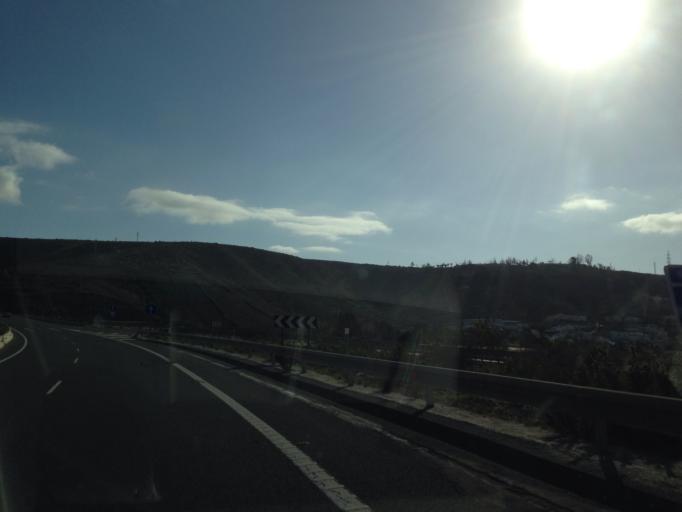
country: ES
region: Canary Islands
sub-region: Provincia de Las Palmas
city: Puerto Rico
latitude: 27.7655
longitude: -15.6723
